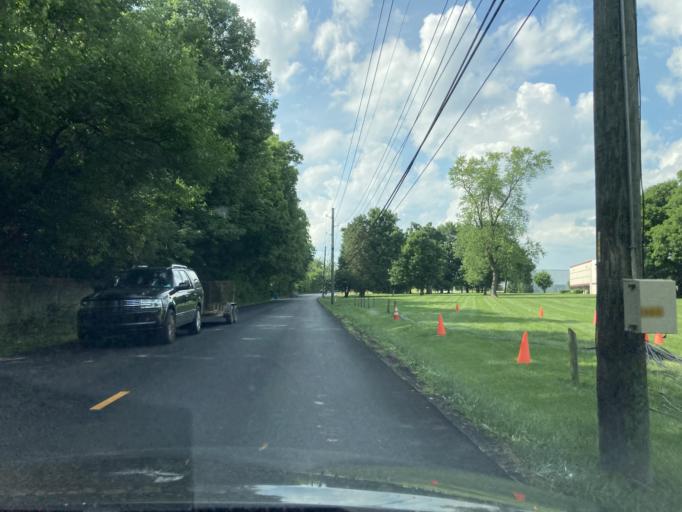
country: US
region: Indiana
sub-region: Marion County
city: Speedway
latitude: 39.8480
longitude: -86.2324
